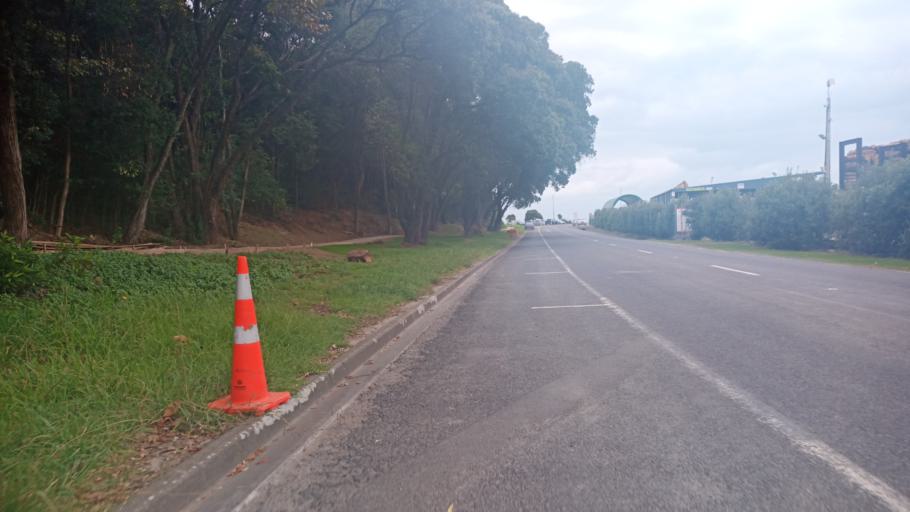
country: NZ
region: Gisborne
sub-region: Gisborne District
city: Gisborne
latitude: -38.6782
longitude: 178.0268
